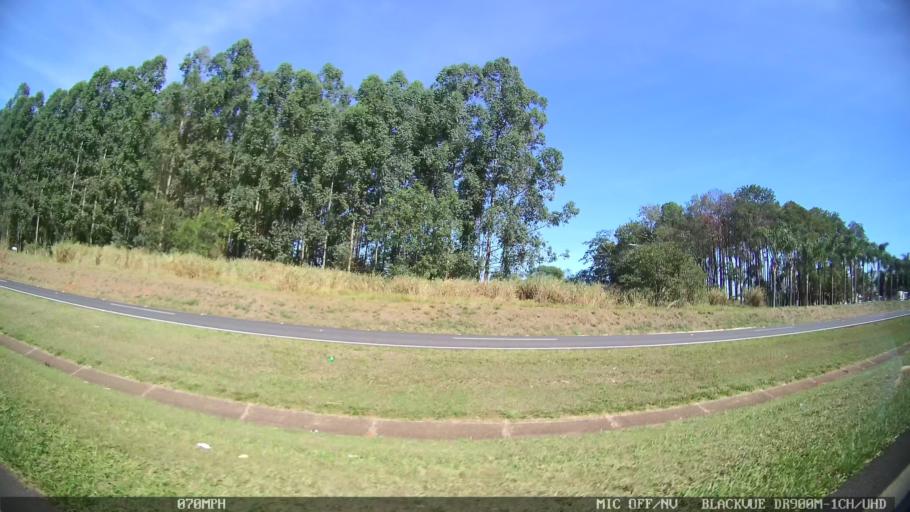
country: BR
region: Sao Paulo
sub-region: Santa Rita Do Passa Quatro
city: Santa Rita do Passa Quatro
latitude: -21.7803
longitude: -47.5327
